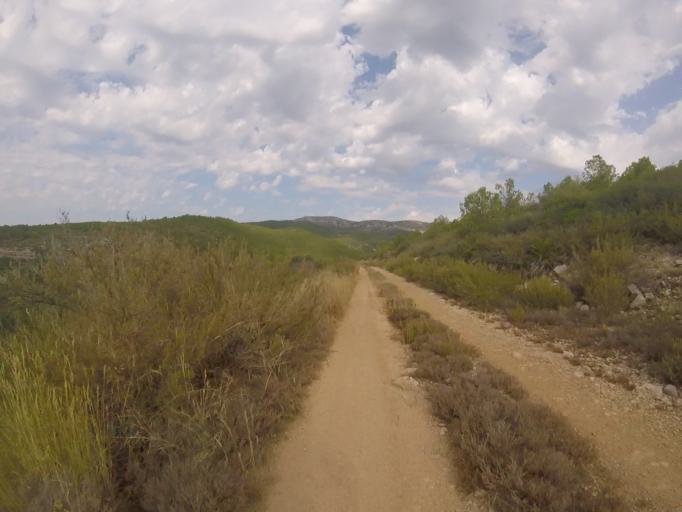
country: ES
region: Valencia
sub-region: Provincia de Castello
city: Alcala de Xivert
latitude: 40.3848
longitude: 0.2089
